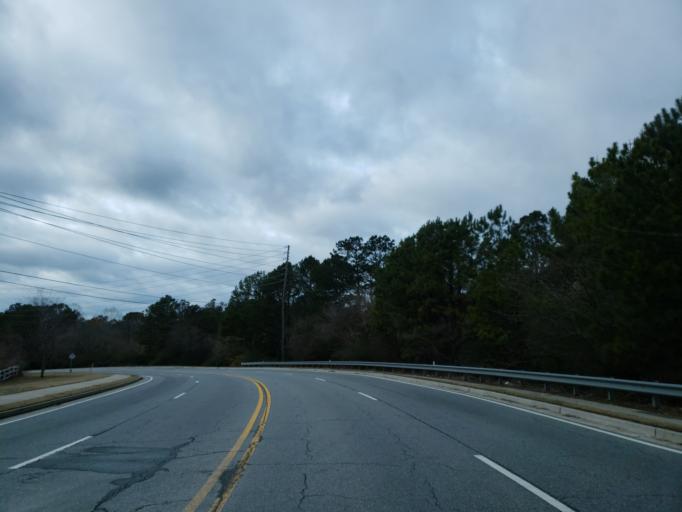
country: US
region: Georgia
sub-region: Cobb County
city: Fair Oaks
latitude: 33.9013
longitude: -84.5770
